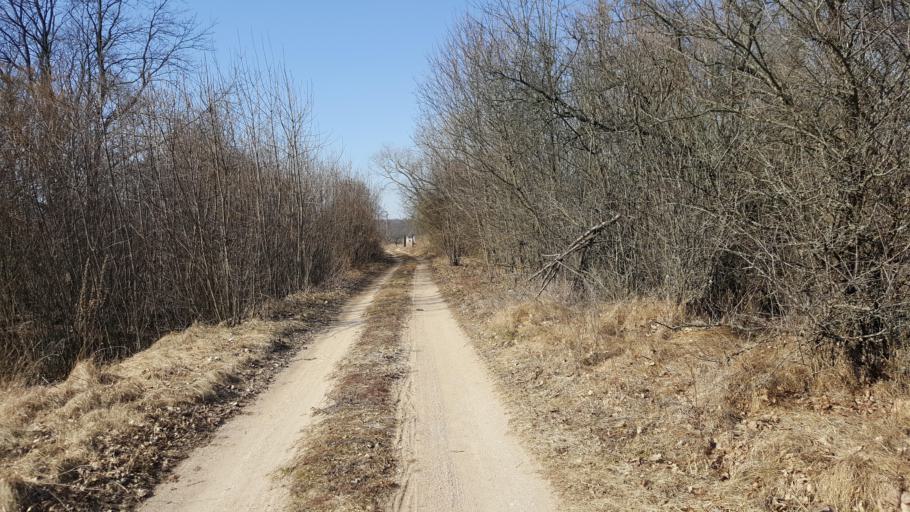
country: BY
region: Brest
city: Kamyanyets
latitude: 52.3619
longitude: 23.7462
